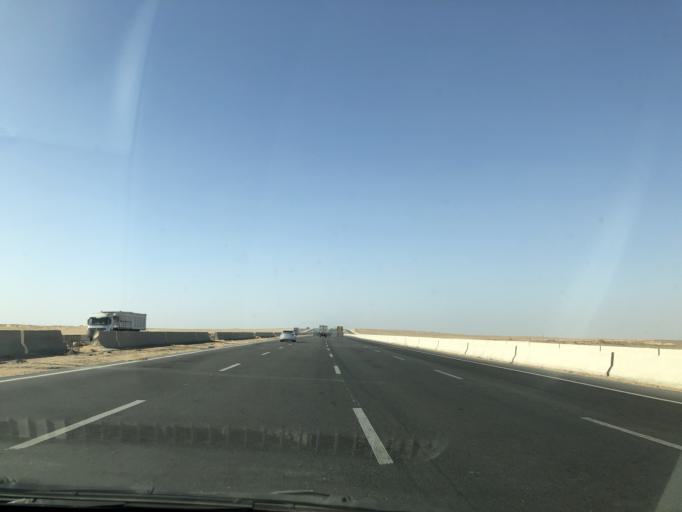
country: EG
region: Al Jizah
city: Madinat Sittah Uktubar
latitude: 30.0151
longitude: 30.8461
